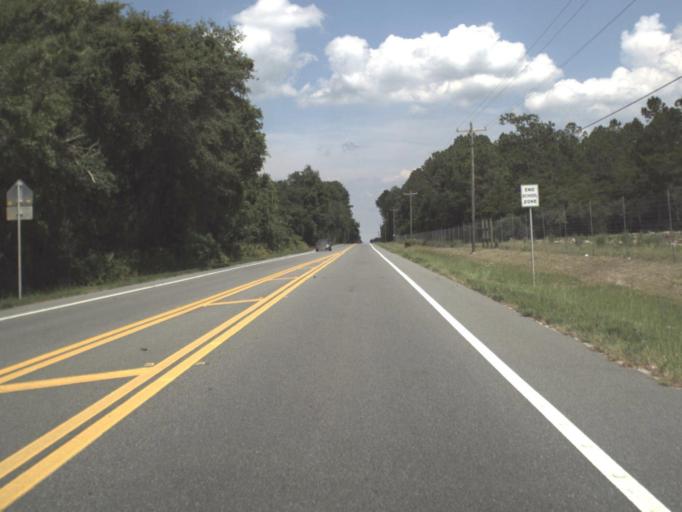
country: US
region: Florida
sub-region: Putnam County
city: Interlachen
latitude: 29.7265
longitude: -81.8439
